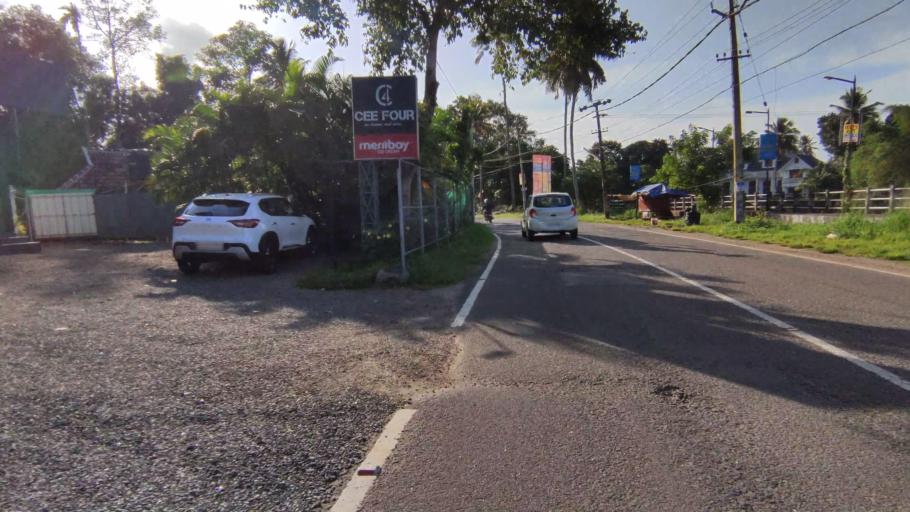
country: IN
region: Kerala
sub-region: Kottayam
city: Kottayam
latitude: 9.5919
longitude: 76.4955
